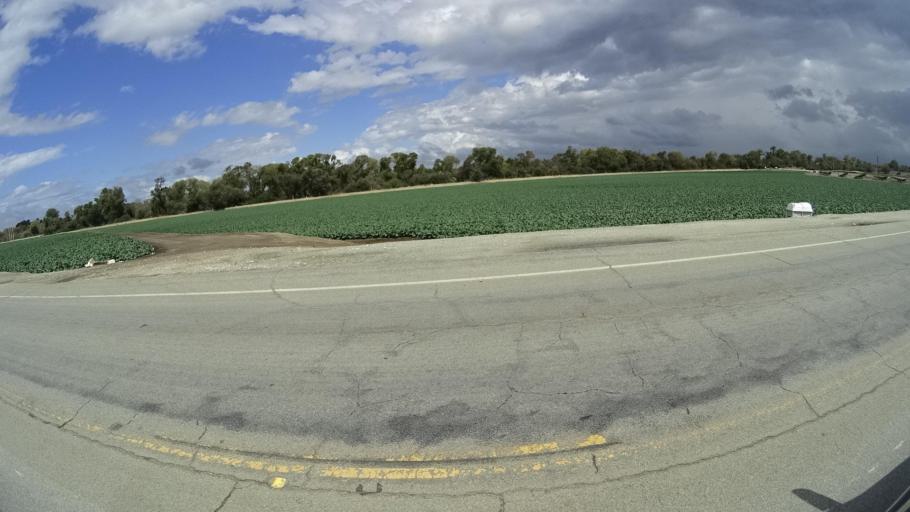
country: US
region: California
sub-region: Monterey County
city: Salinas
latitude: 36.6257
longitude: -121.6850
